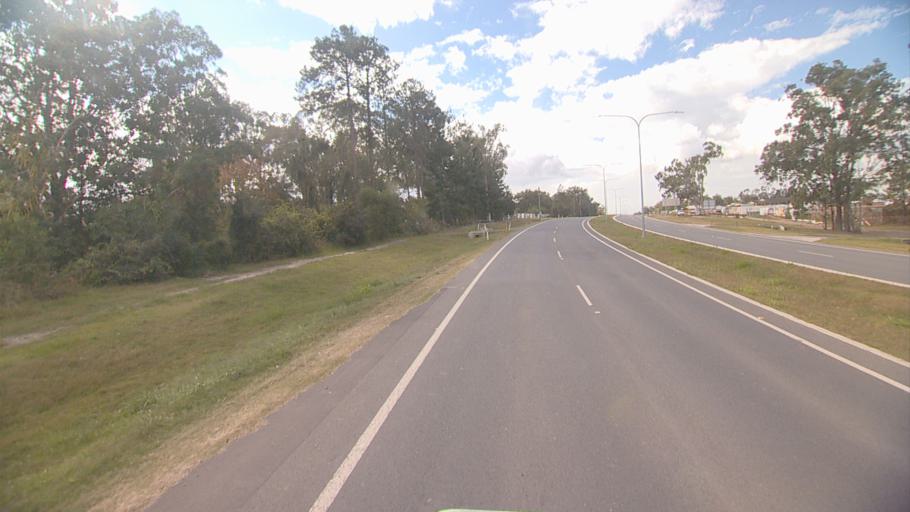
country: AU
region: Queensland
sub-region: Logan
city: Logan Reserve
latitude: -27.7068
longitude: 153.0941
